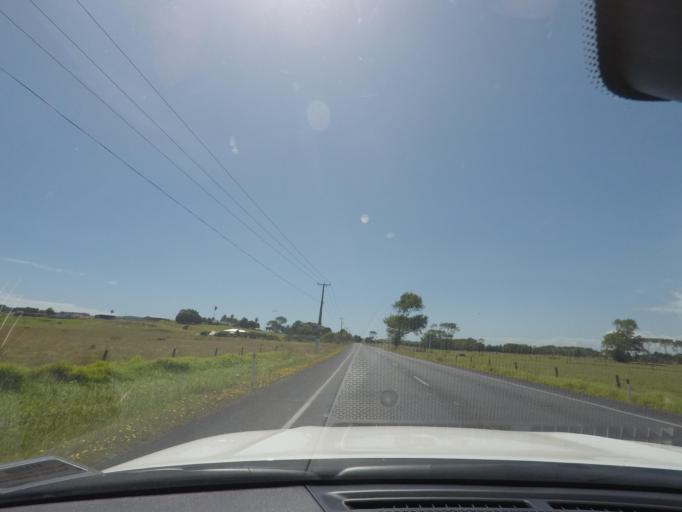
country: NZ
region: Auckland
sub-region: Auckland
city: Parakai
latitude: -36.7024
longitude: 174.4370
